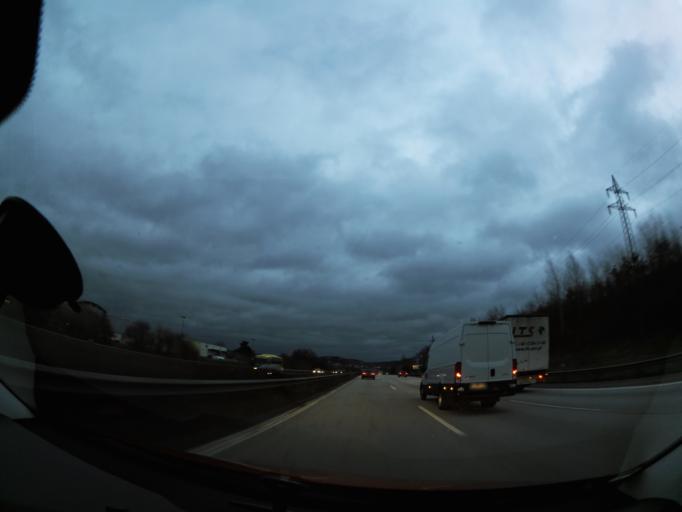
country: DE
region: Rheinland-Pfalz
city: Heiligenroth
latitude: 50.4496
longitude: 7.8554
